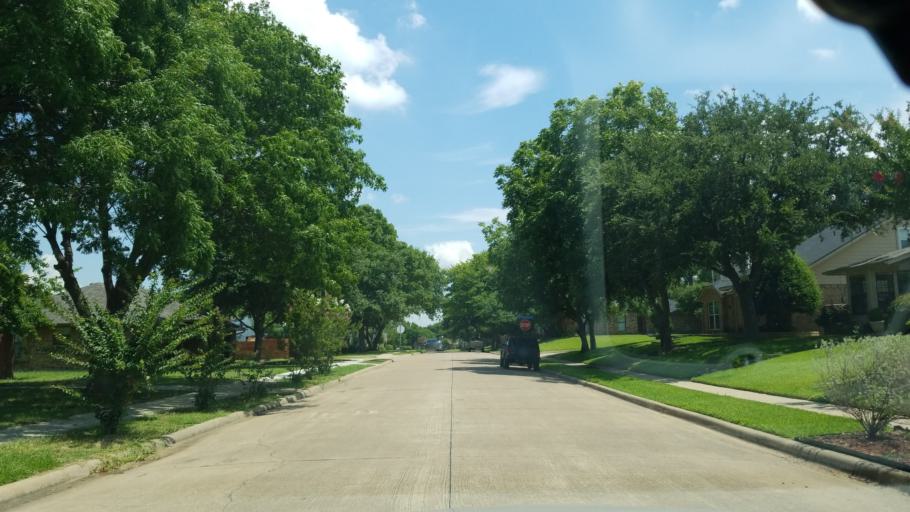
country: US
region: Texas
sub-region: Dallas County
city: Coppell
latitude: 32.9642
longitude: -96.9641
